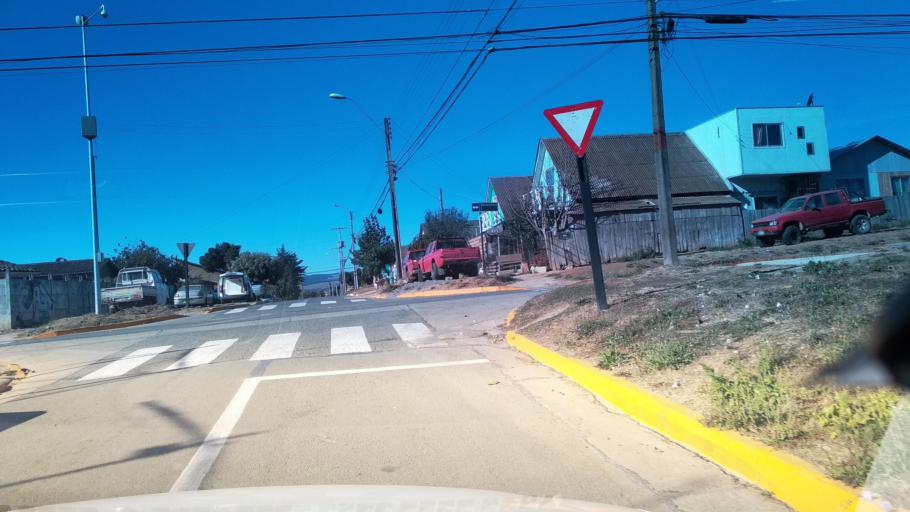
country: CL
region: O'Higgins
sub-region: Provincia de Colchagua
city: Santa Cruz
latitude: -34.3907
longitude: -72.0083
